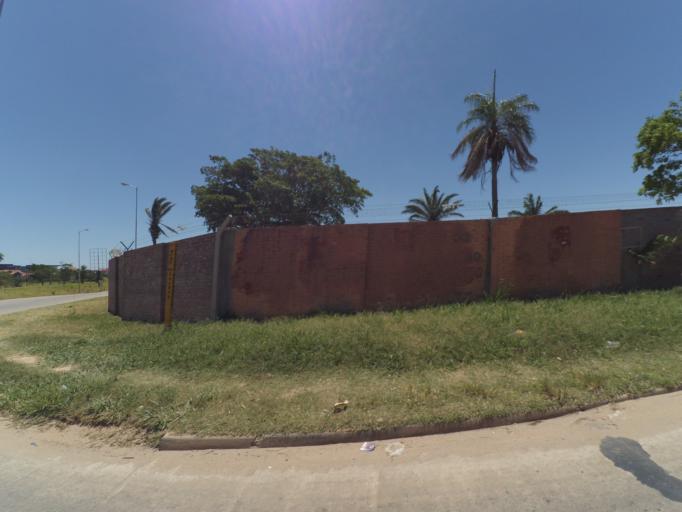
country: BO
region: Santa Cruz
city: Santa Cruz de la Sierra
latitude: -17.7555
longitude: -63.2214
